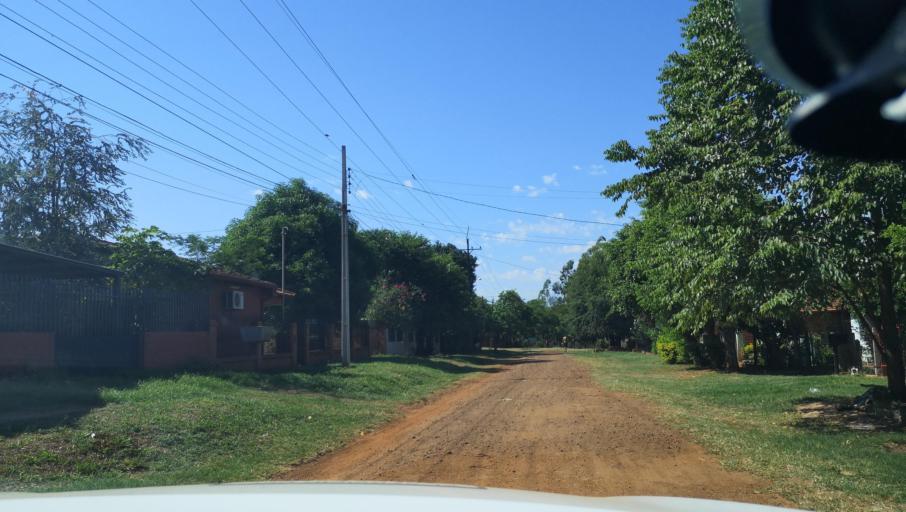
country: PY
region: Itapua
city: Carmen del Parana
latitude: -27.1707
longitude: -56.2345
